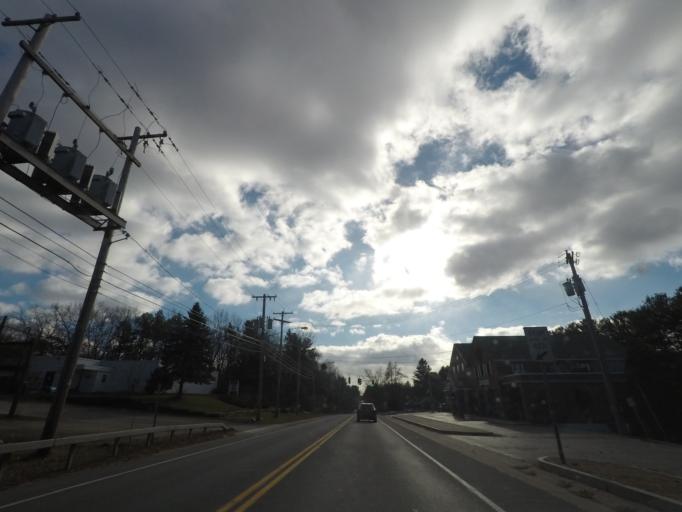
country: US
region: New York
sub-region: Schenectady County
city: Schenectady
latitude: 42.8059
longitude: -73.8930
